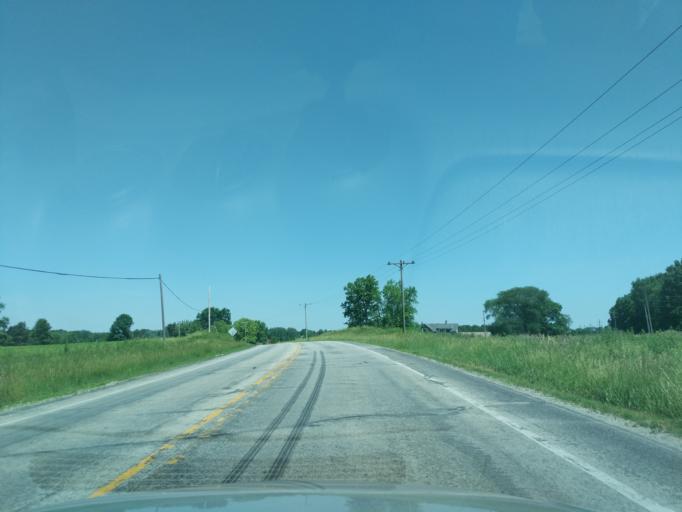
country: US
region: Indiana
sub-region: Whitley County
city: Columbia City
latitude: 41.1166
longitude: -85.4718
